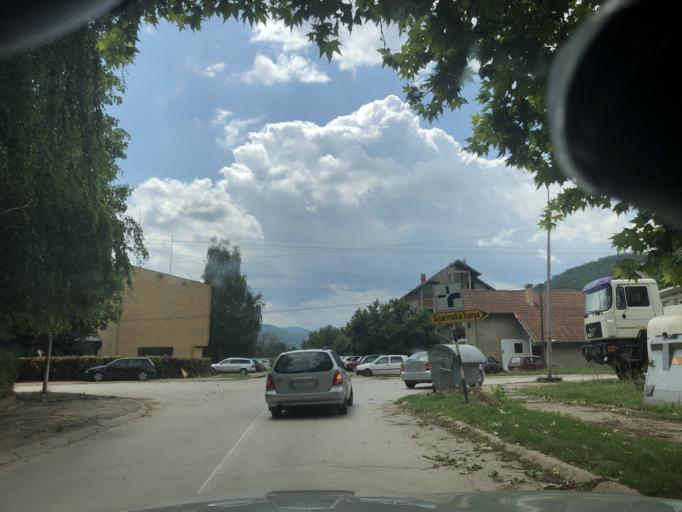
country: RS
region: Central Serbia
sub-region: Jablanicki Okrug
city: Medvega
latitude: 42.8397
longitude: 21.5859
